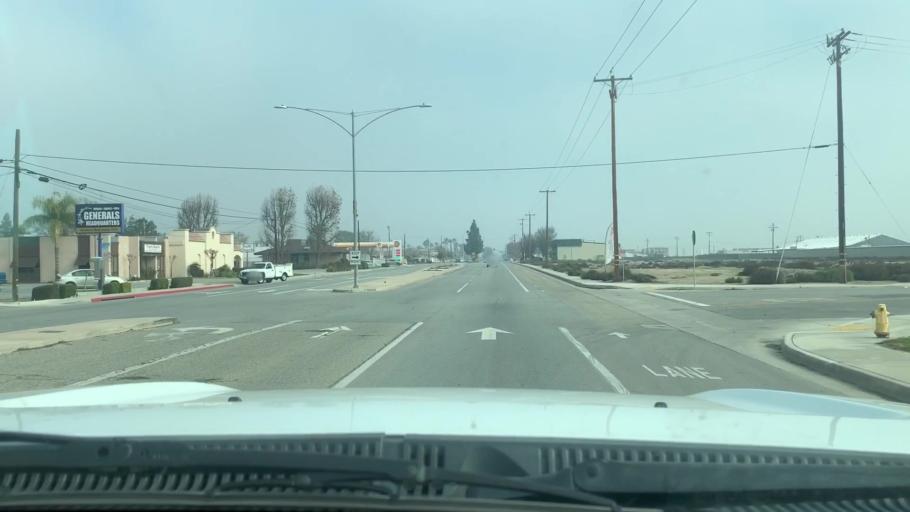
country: US
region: California
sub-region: Kern County
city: Shafter
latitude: 35.4998
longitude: -119.2652
